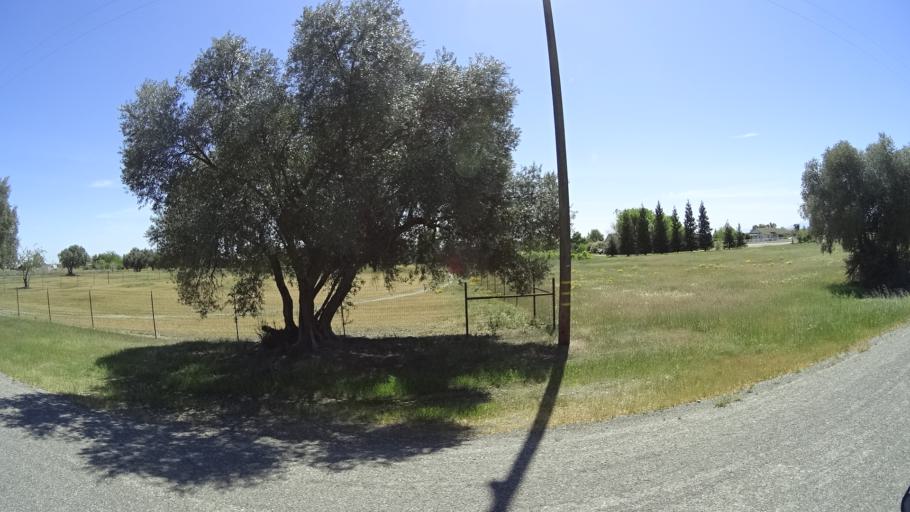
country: US
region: California
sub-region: Glenn County
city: Orland
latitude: 39.7416
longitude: -122.1605
